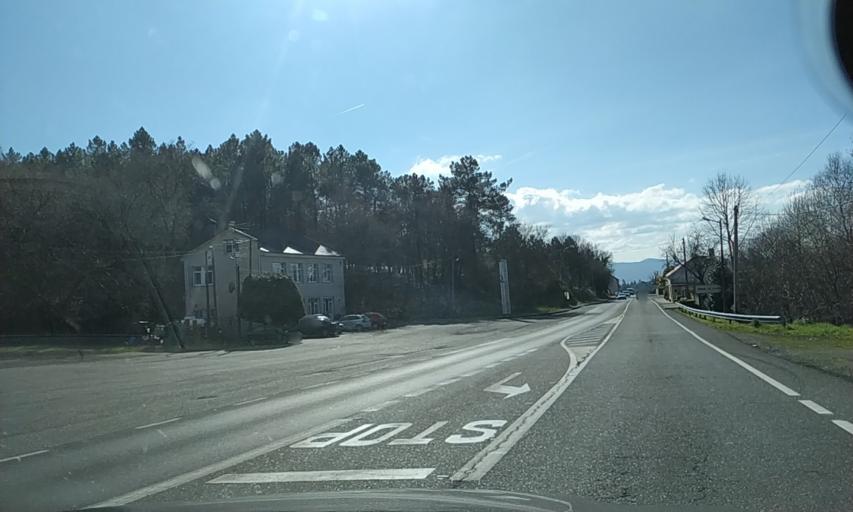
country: ES
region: Galicia
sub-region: Provincia da Coruna
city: Ribeira
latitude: 42.7077
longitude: -8.3944
